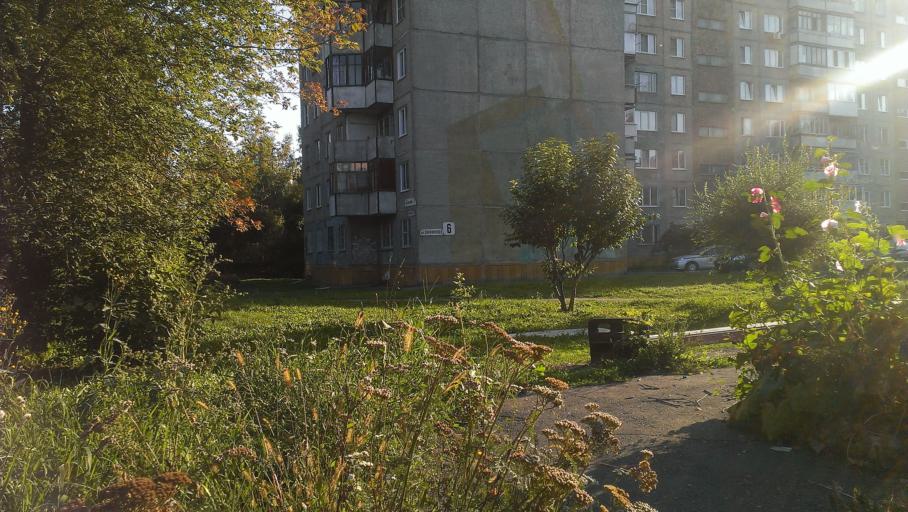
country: RU
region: Altai Krai
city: Novosilikatnyy
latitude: 53.3532
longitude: 83.6767
